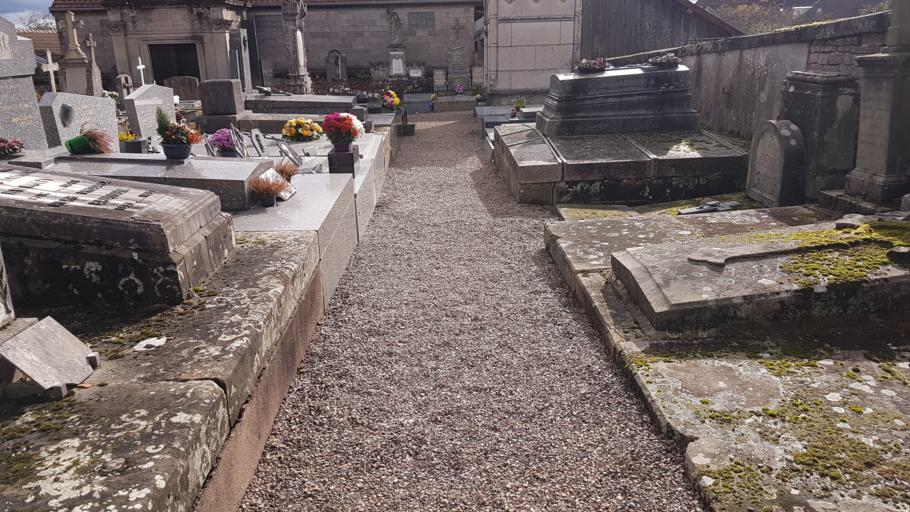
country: FR
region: Franche-Comte
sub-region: Departement de la Haute-Saone
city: Saint-Sauveur
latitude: 47.8193
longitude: 6.3824
